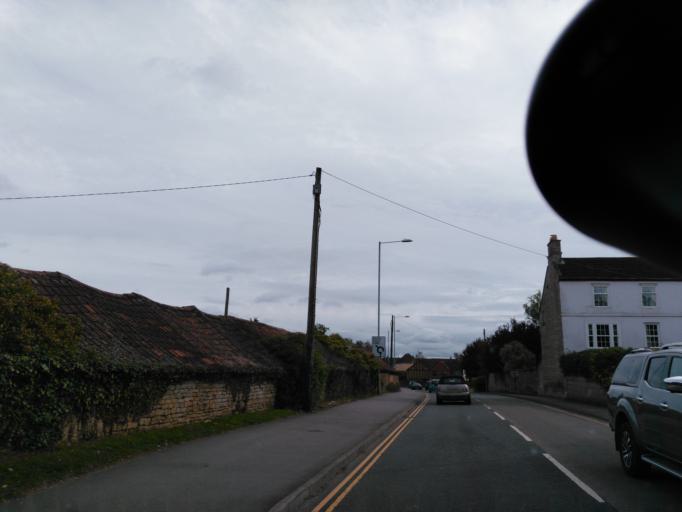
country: GB
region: England
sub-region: Wiltshire
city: Melksham
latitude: 51.3611
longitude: -2.1220
